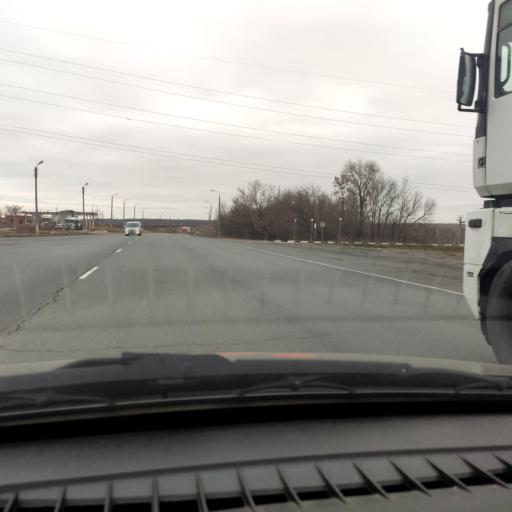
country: RU
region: Samara
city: Zhigulevsk
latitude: 53.3627
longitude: 49.4579
